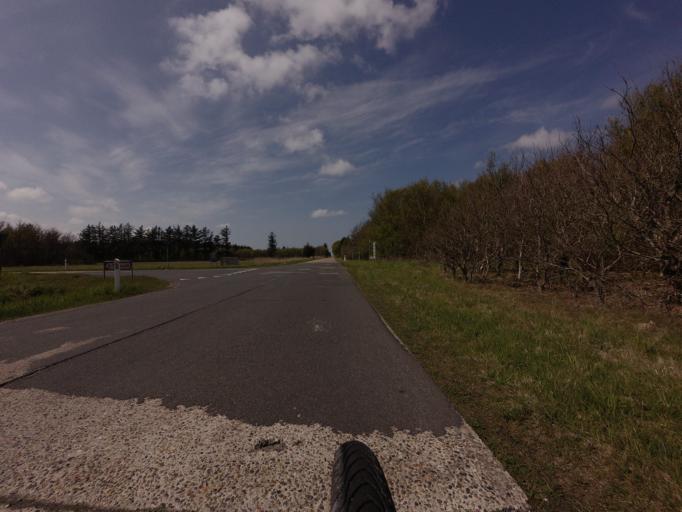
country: DK
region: North Denmark
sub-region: Jammerbugt Kommune
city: Brovst
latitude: 57.1663
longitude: 9.4773
